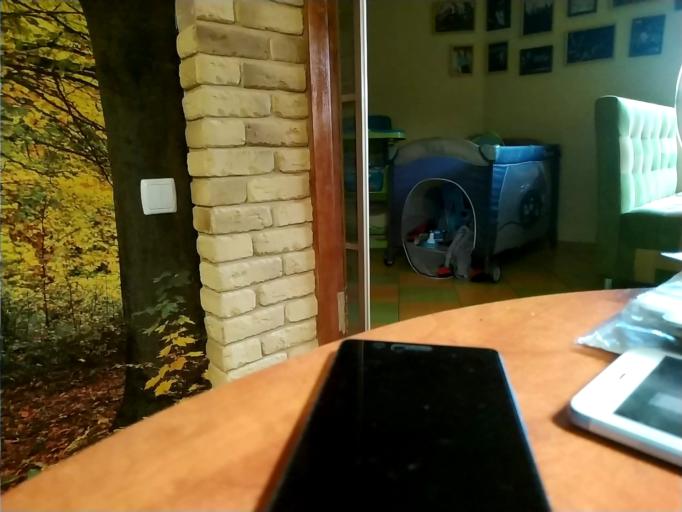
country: RU
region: Kaluga
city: Khvastovichi
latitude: 53.6531
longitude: 35.4492
